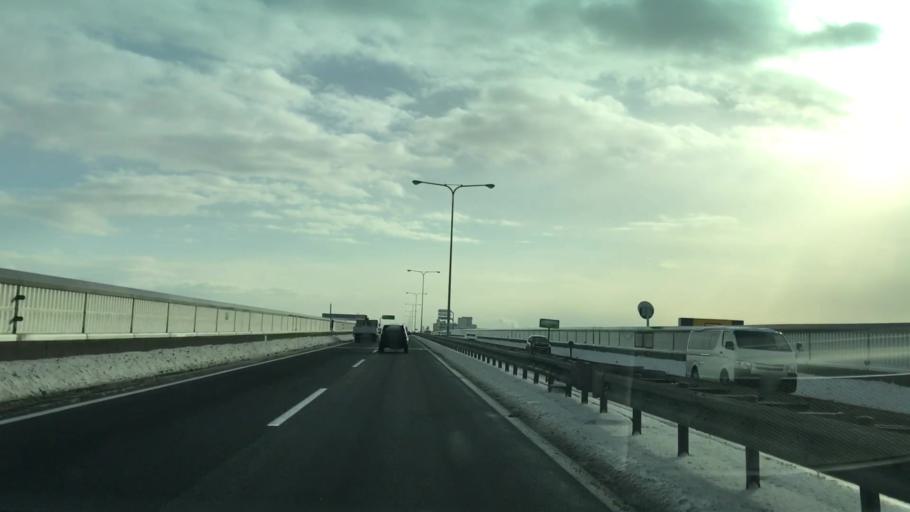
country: JP
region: Hokkaido
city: Sapporo
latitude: 43.1011
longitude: 141.3846
